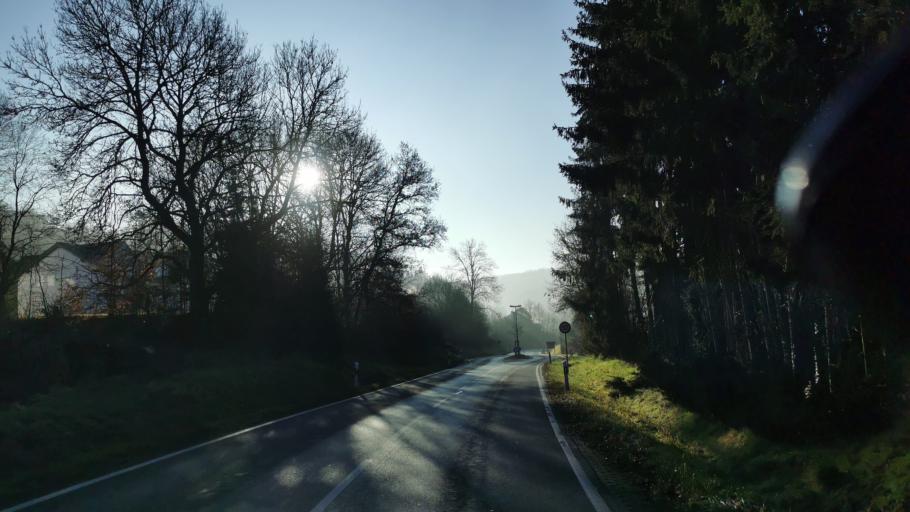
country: DE
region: Rheinland-Pfalz
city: Daun
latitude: 50.1948
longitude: 6.8118
